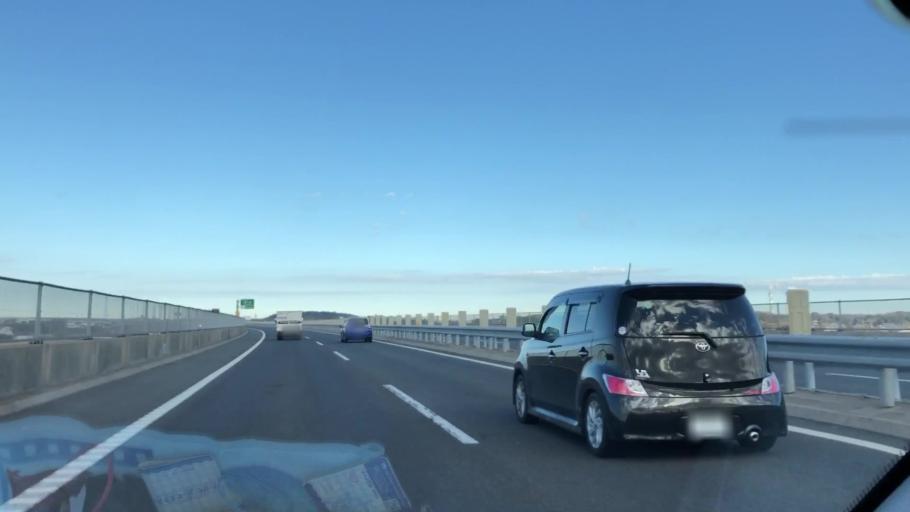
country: JP
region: Chiba
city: Kisarazu
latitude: 35.4026
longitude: 139.9661
